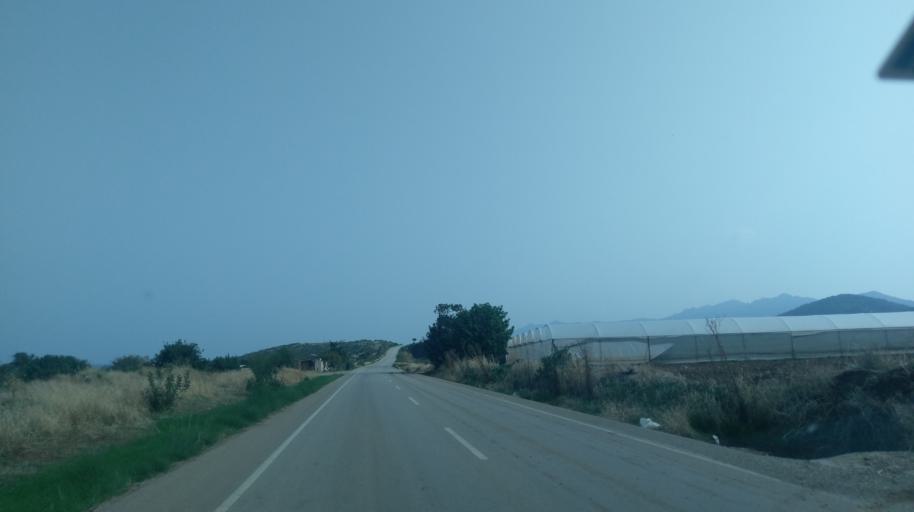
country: CY
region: Ammochostos
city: Lefkonoiko
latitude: 35.4061
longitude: 33.7750
